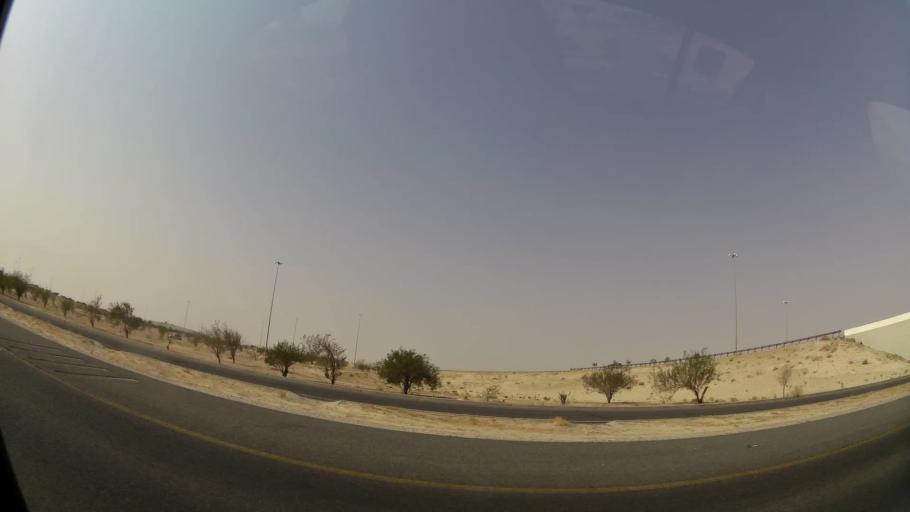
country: KW
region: Muhafazat al Jahra'
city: Al Jahra'
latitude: 29.3416
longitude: 47.6299
